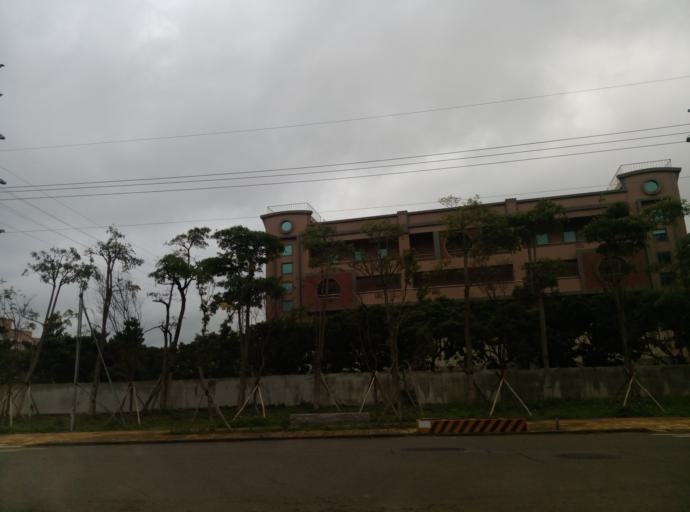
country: TW
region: Taiwan
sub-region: Hsinchu
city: Hsinchu
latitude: 24.6864
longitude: 120.8968
